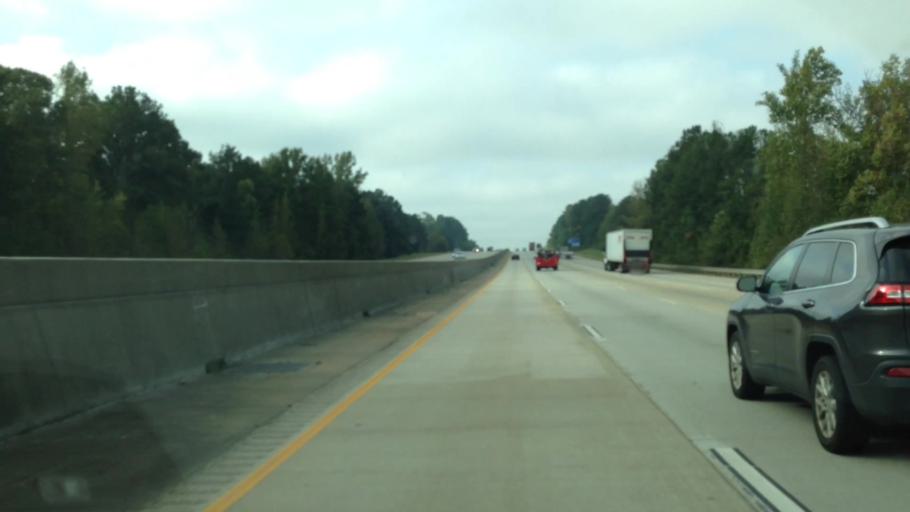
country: US
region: Georgia
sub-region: Coweta County
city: Newnan
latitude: 33.4236
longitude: -84.7266
